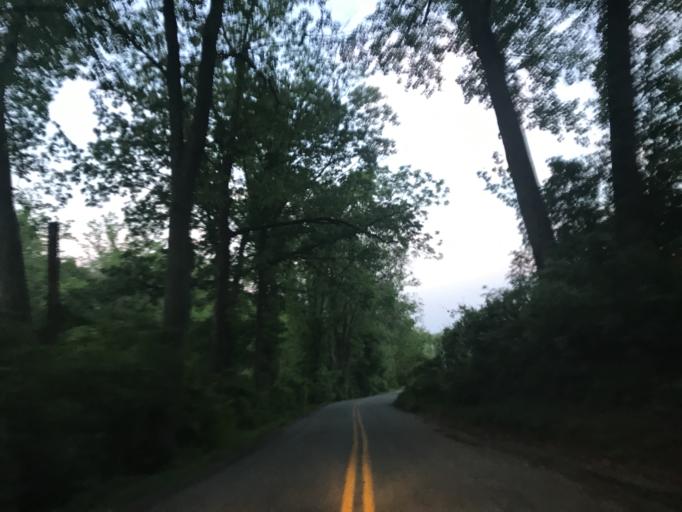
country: US
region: Maryland
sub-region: Harford County
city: Joppatowne
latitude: 39.4655
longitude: -76.3316
